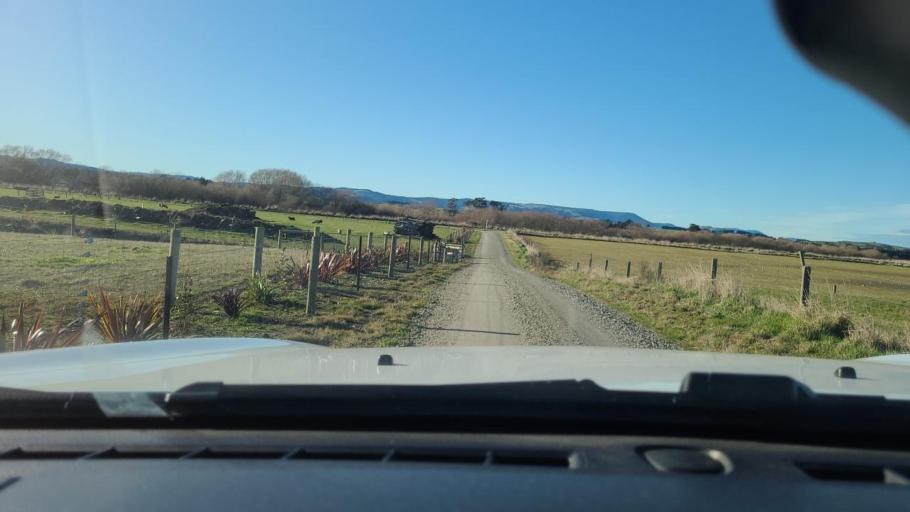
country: NZ
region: Southland
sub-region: Gore District
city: Gore
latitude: -46.3265
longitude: 168.8256
